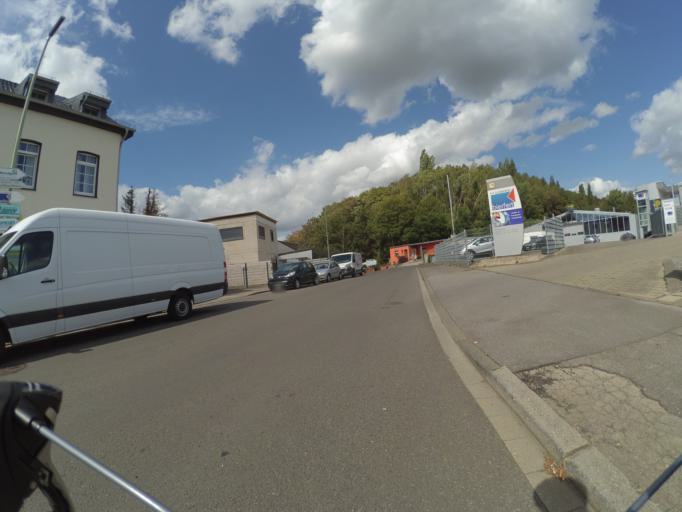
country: DE
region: North Rhine-Westphalia
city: Stolberg
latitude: 50.7884
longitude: 6.2104
